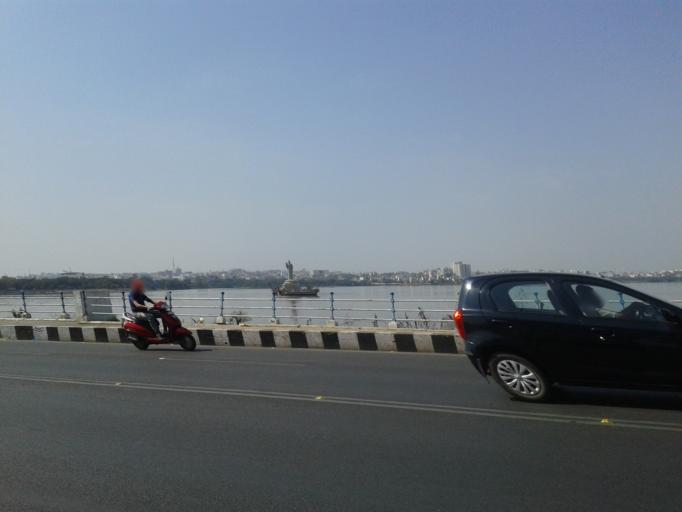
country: IN
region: Telangana
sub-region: Hyderabad
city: Hyderabad
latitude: 17.4151
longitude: 78.4794
